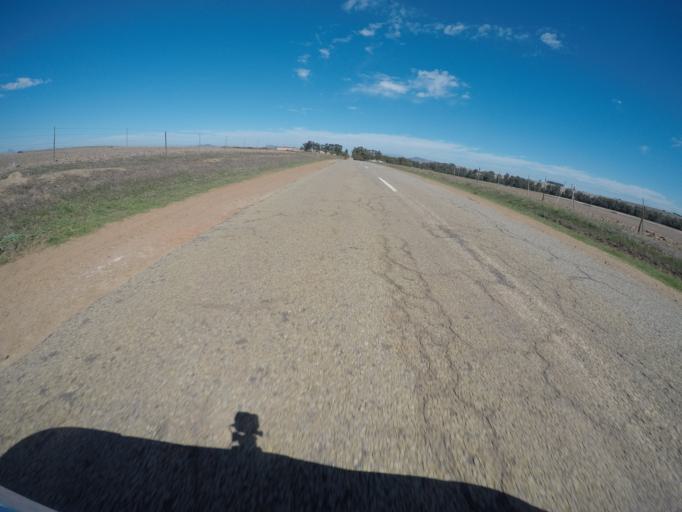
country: ZA
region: Western Cape
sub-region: City of Cape Town
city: Atlantis
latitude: -33.6069
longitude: 18.6389
